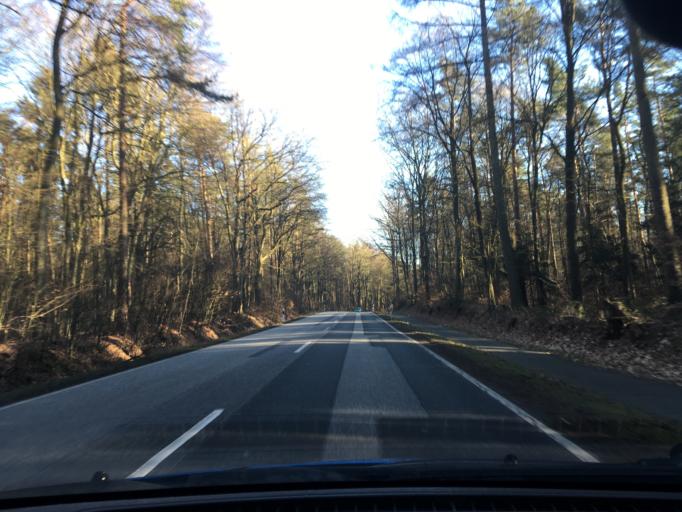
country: DE
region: Schleswig-Holstein
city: Schnakenbek
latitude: 53.3805
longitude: 10.5105
